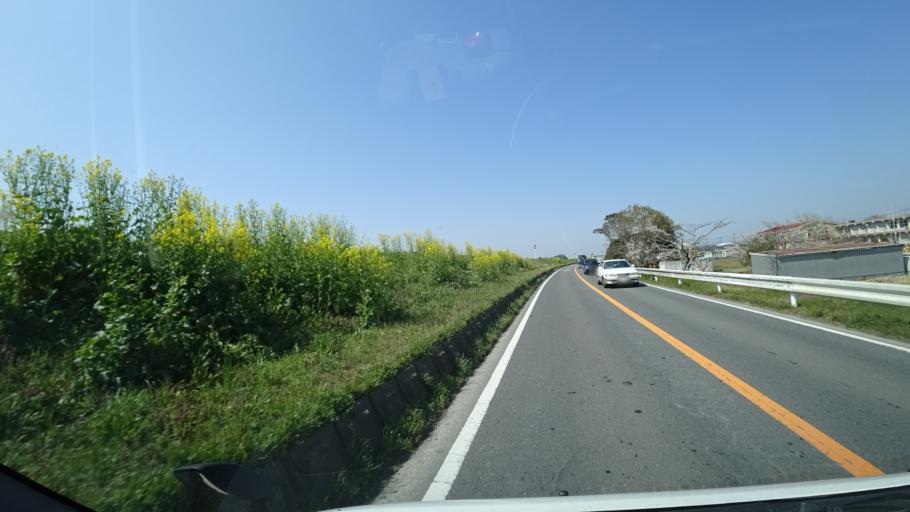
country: JP
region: Chiba
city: Katori-shi
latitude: 35.9101
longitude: 140.4236
